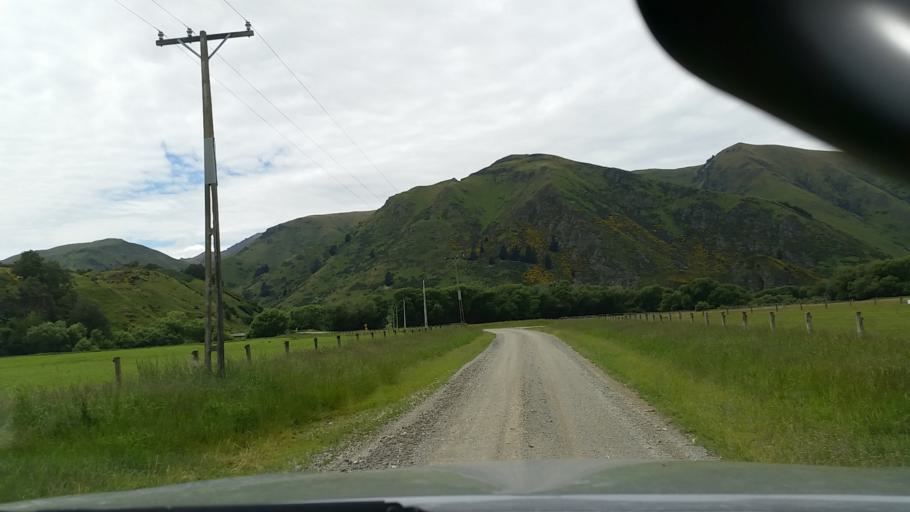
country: NZ
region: Otago
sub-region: Queenstown-Lakes District
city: Kingston
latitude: -45.5586
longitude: 168.6365
